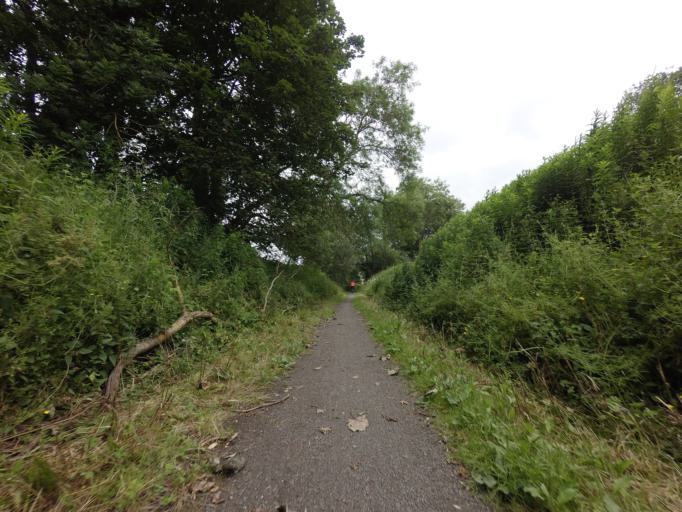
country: GB
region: Scotland
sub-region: Aberdeenshire
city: Mintlaw
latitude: 57.5128
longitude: -2.1396
